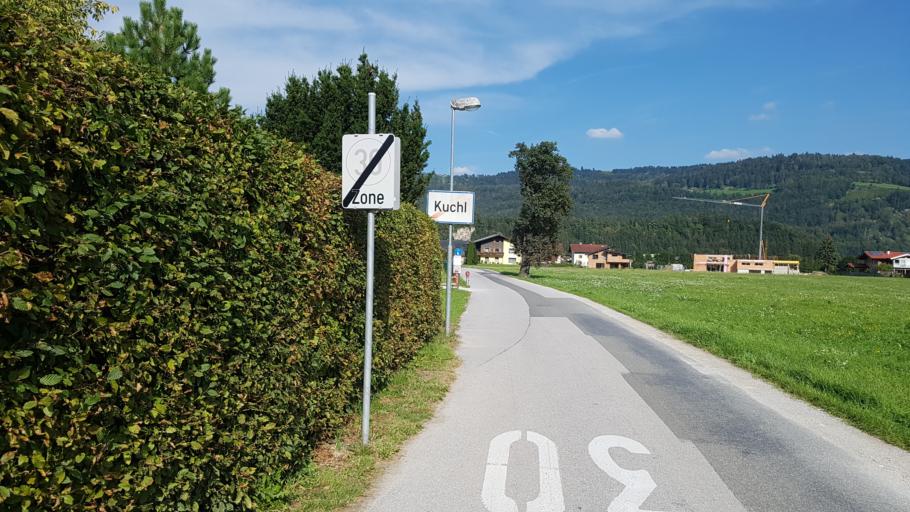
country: AT
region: Salzburg
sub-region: Politischer Bezirk Hallein
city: Kuchl
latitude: 47.6290
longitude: 13.1515
